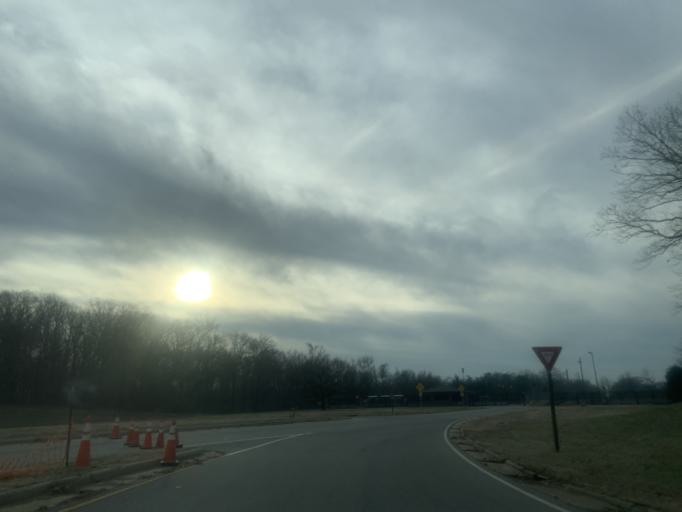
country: US
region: Maryland
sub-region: Prince George's County
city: Forestville
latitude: 38.8290
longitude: -76.8591
